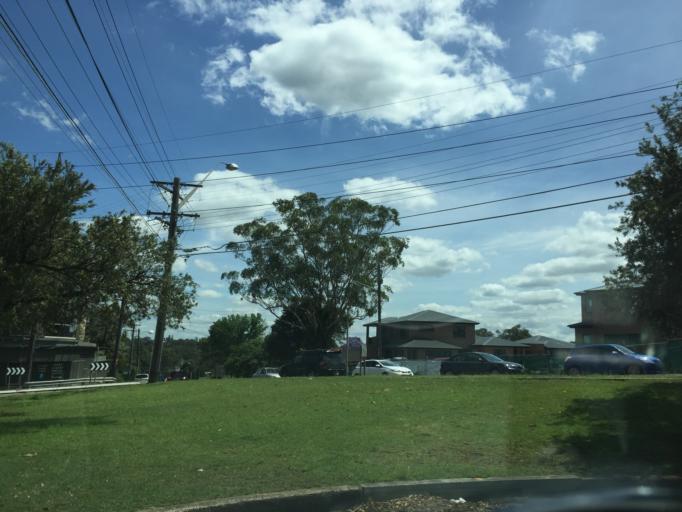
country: AU
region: New South Wales
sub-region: Ryde
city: Denistone
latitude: -33.7908
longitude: 151.0864
